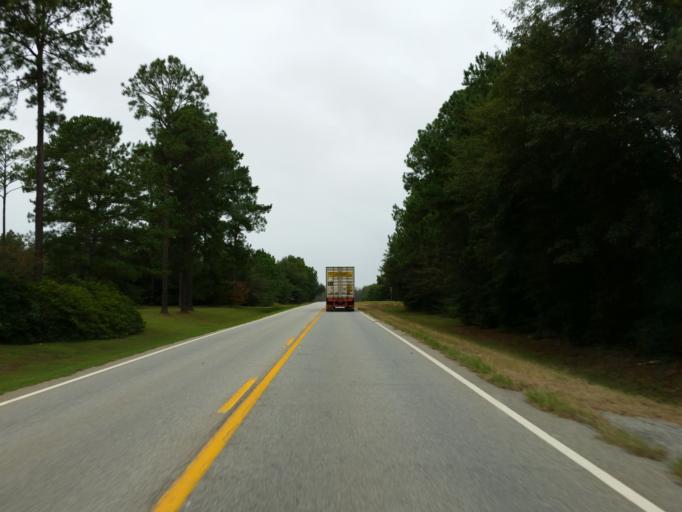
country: US
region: Georgia
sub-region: Berrien County
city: Ray City
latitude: 31.0868
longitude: -83.2407
